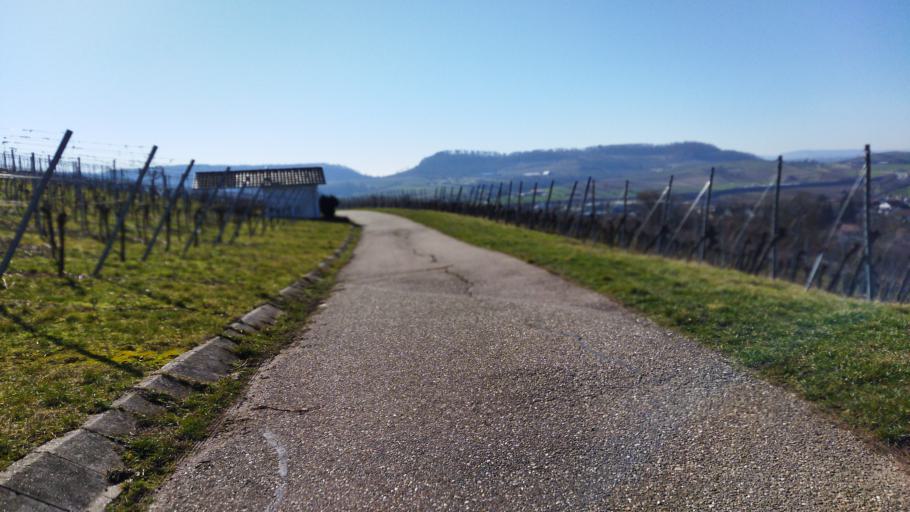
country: DE
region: Baden-Wuerttemberg
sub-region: Regierungsbezirk Stuttgart
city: Erlenbach
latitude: 49.1746
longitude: 9.2731
